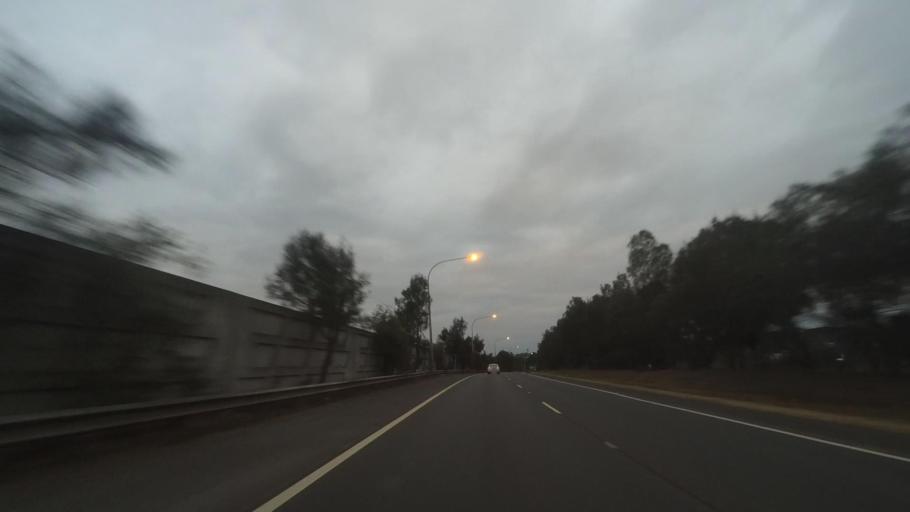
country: AU
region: New South Wales
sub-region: Wollongong
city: Mount Saint Thomas
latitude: -34.4457
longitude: 150.8607
